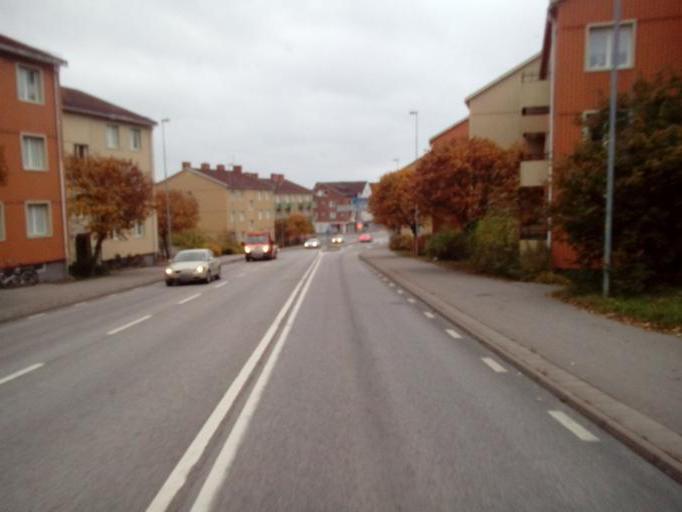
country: SE
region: OErebro
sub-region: Degerfors Kommun
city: Degerfors
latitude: 59.2391
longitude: 14.4338
